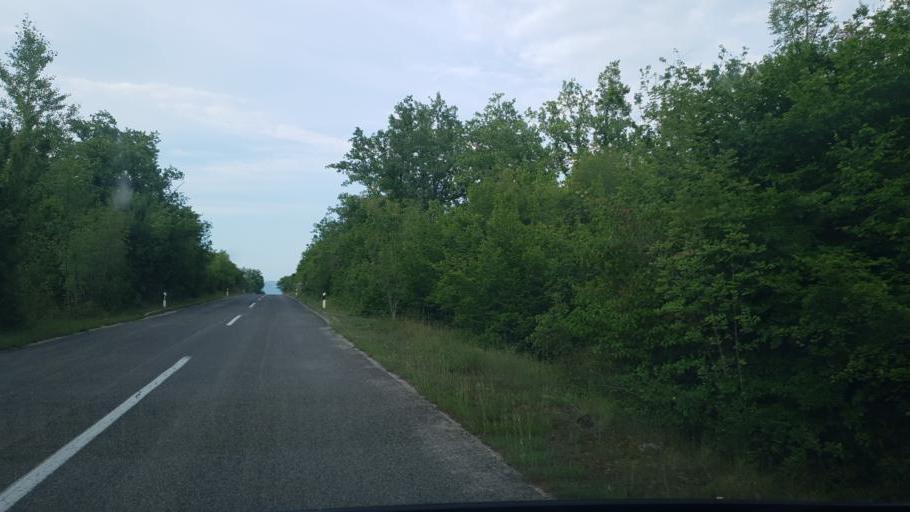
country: HR
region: Primorsko-Goranska
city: Njivice
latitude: 45.1289
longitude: 14.5771
